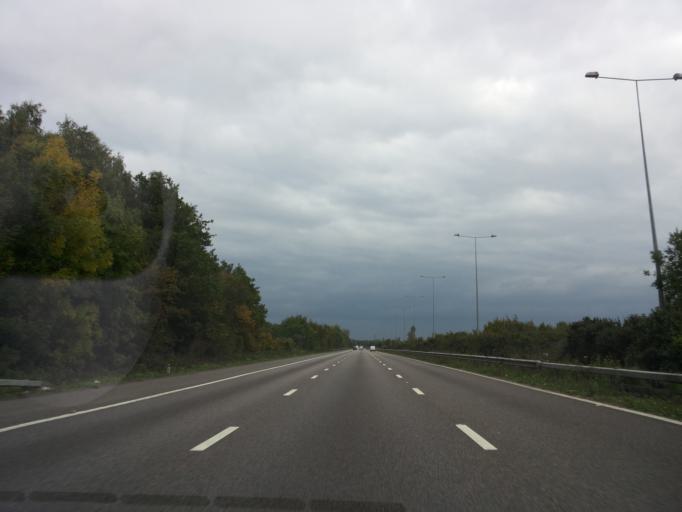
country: GB
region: England
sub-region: Kent
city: Boxley
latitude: 51.3258
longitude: 0.5391
